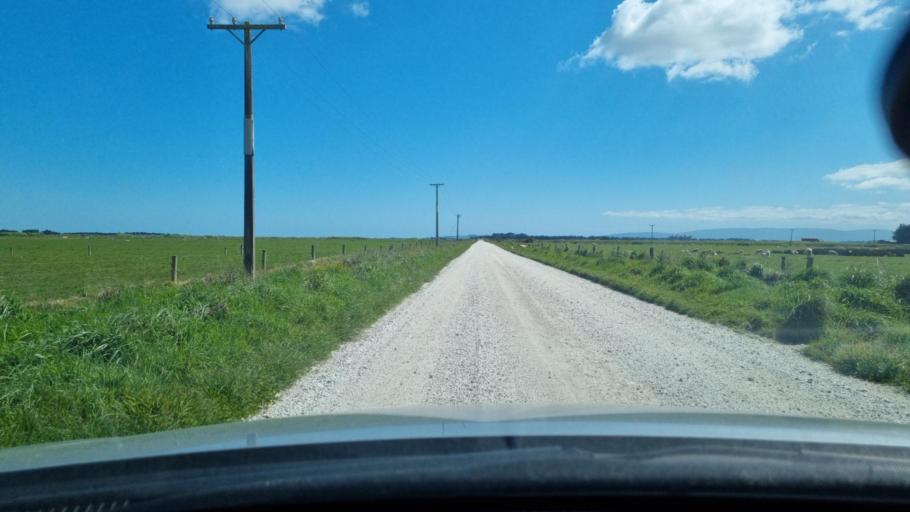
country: NZ
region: Southland
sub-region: Invercargill City
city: Invercargill
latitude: -46.3693
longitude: 168.2628
